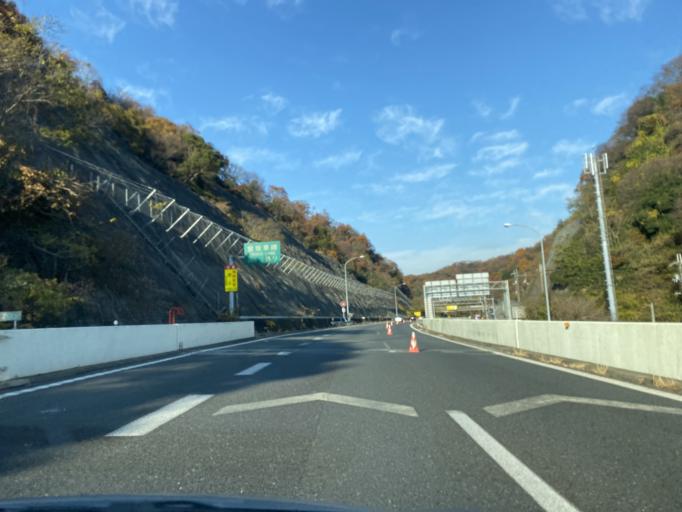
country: JP
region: Wakayama
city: Iwade
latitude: 34.2921
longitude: 135.2704
